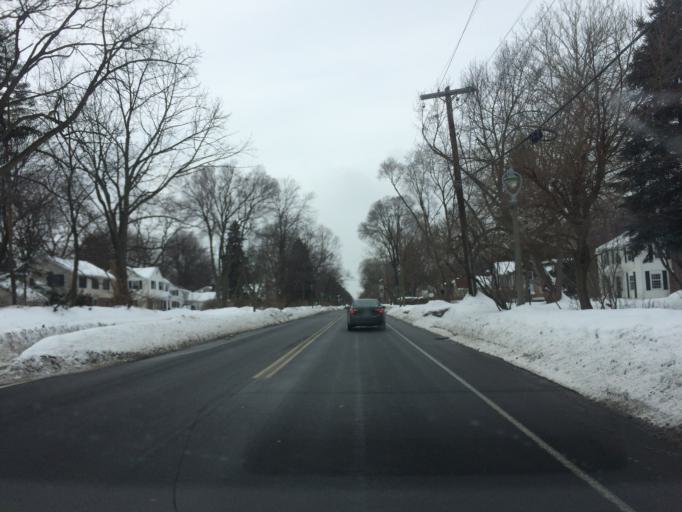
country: US
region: New York
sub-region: Monroe County
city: Brighton
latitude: 43.1268
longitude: -77.5558
